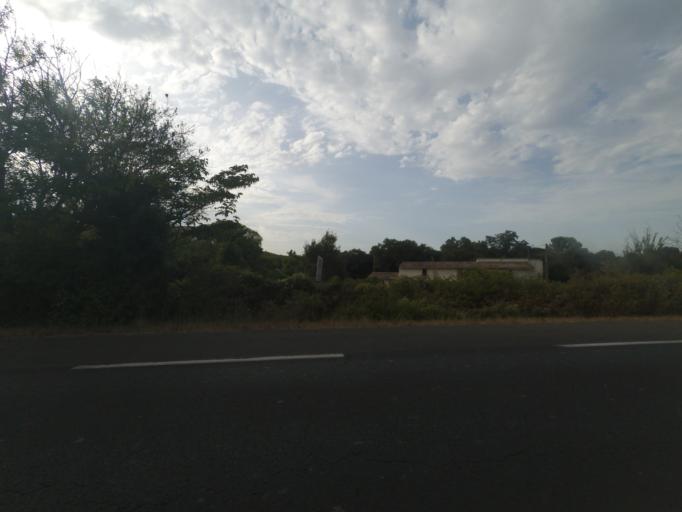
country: FR
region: Languedoc-Roussillon
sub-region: Departement de l'Herault
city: Sussargues
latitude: 43.6969
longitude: 4.0150
